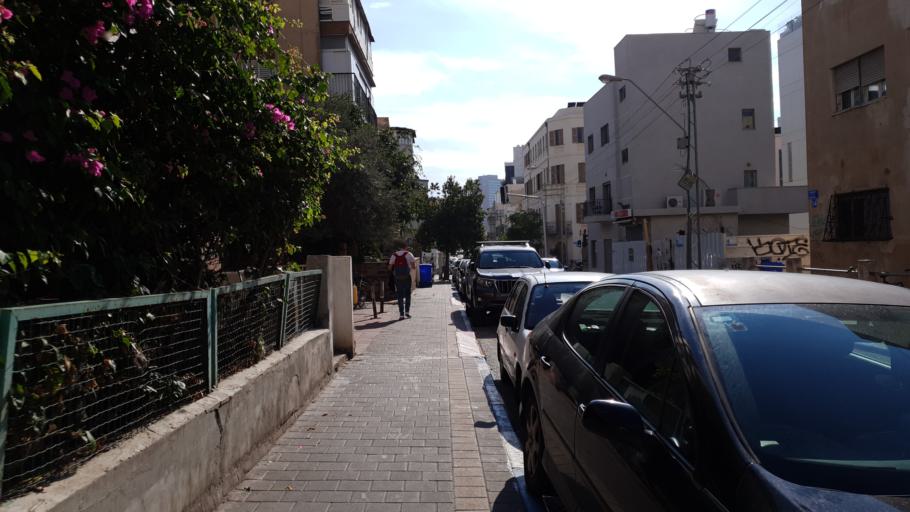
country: IL
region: Tel Aviv
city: Tel Aviv
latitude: 32.0716
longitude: 34.7673
